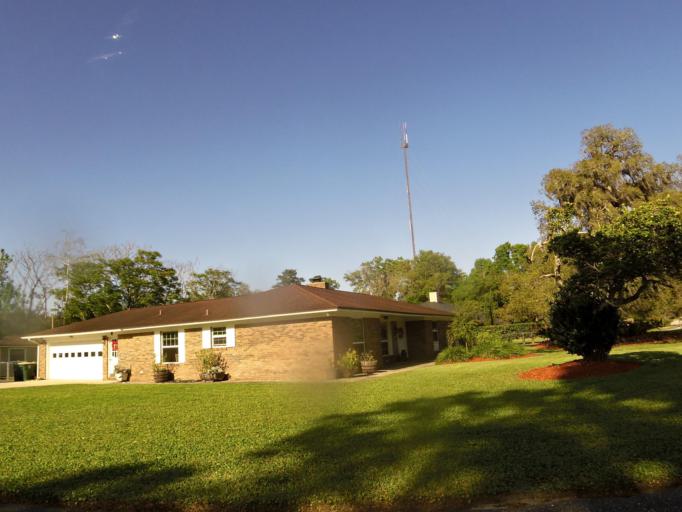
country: US
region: Florida
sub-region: Duval County
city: Jacksonville
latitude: 30.2776
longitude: -81.5756
